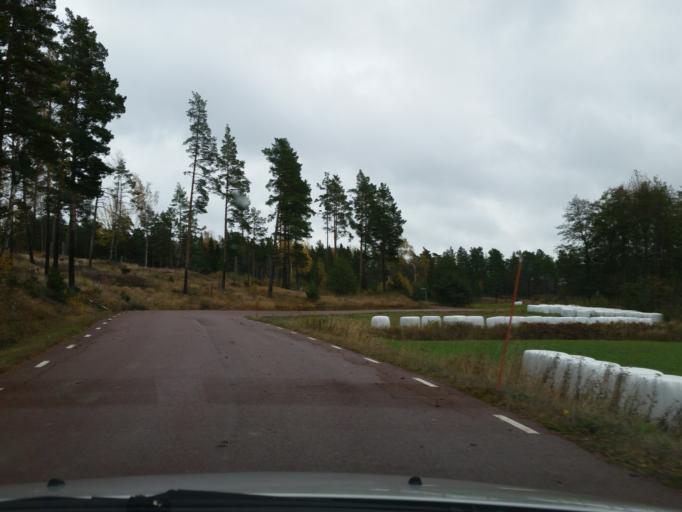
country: AX
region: Alands landsbygd
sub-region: Lumparland
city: Lumparland
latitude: 60.1341
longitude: 20.2727
